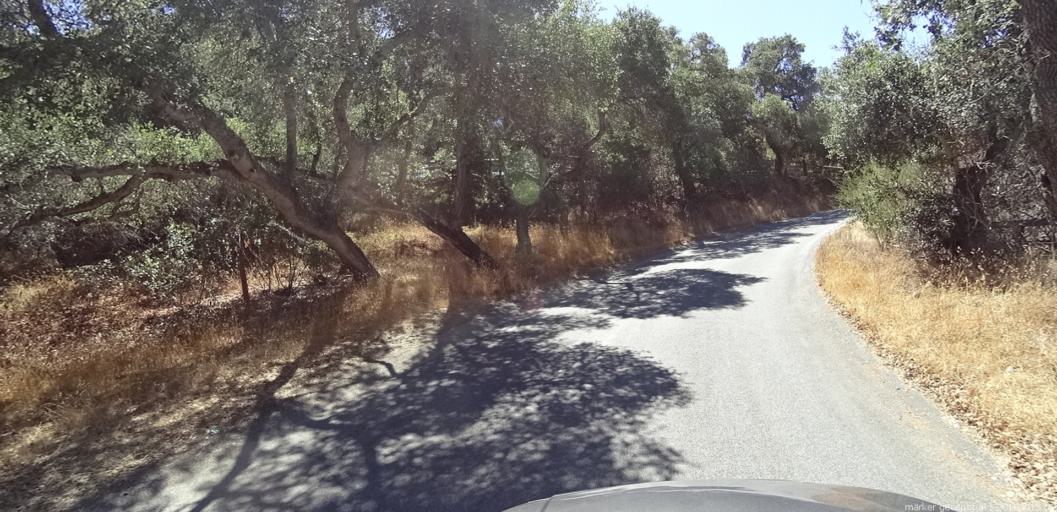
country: US
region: California
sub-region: Monterey County
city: Carmel Valley Village
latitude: 36.5098
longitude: -121.7598
